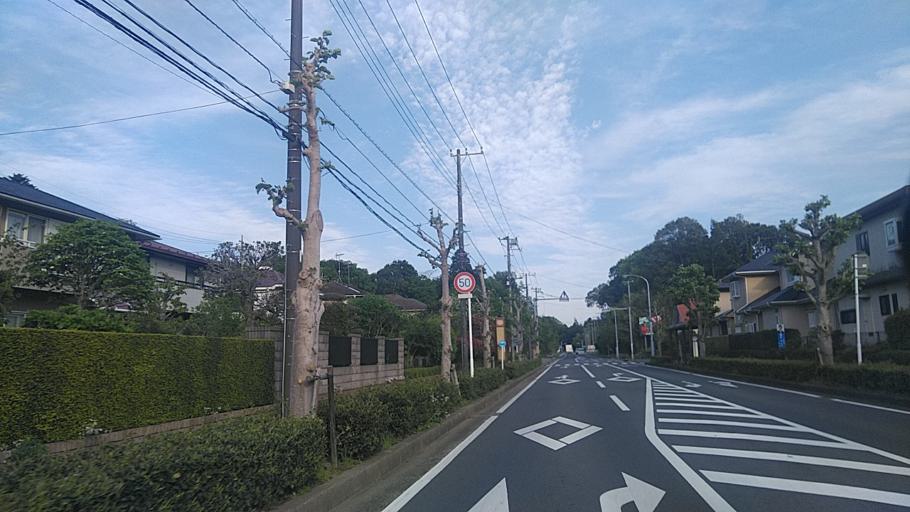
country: JP
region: Chiba
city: Shiroi
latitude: 35.7916
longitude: 140.1443
